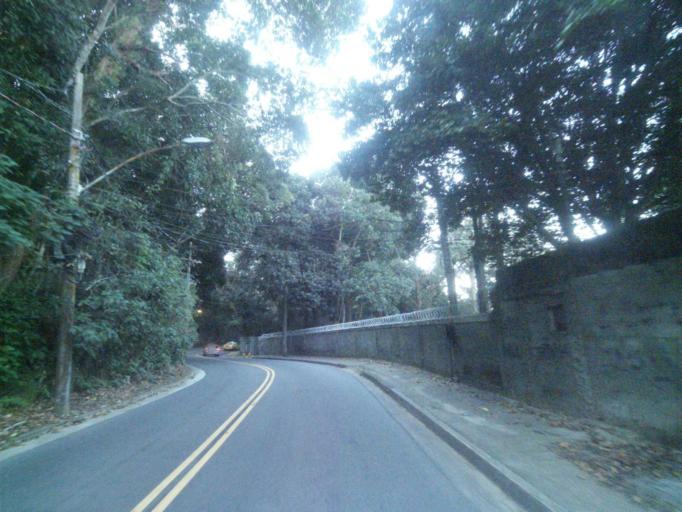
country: BR
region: Rio de Janeiro
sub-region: Rio De Janeiro
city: Rio de Janeiro
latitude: -23.0045
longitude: -43.2811
